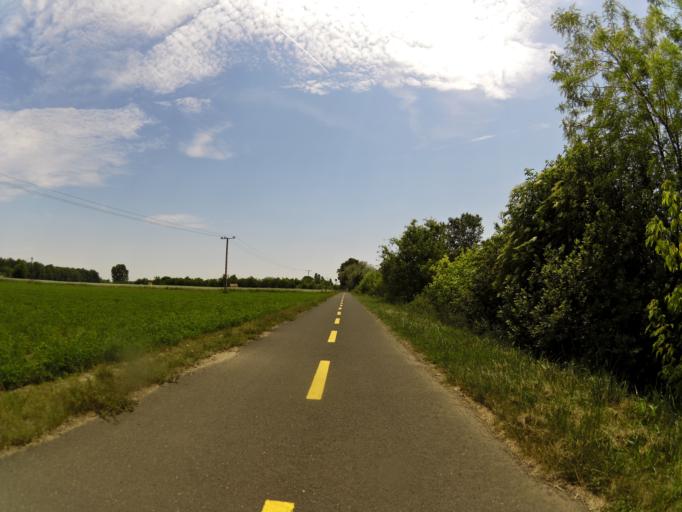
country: HU
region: Csongrad
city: Kistelek
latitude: 46.4517
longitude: 19.9962
